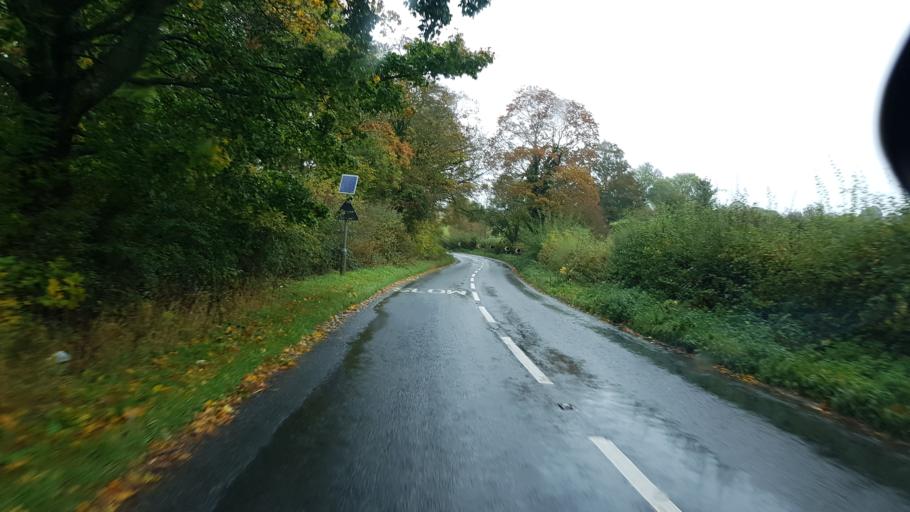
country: GB
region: England
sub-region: Gloucestershire
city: Stow on the Wold
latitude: 51.9385
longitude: -1.7413
